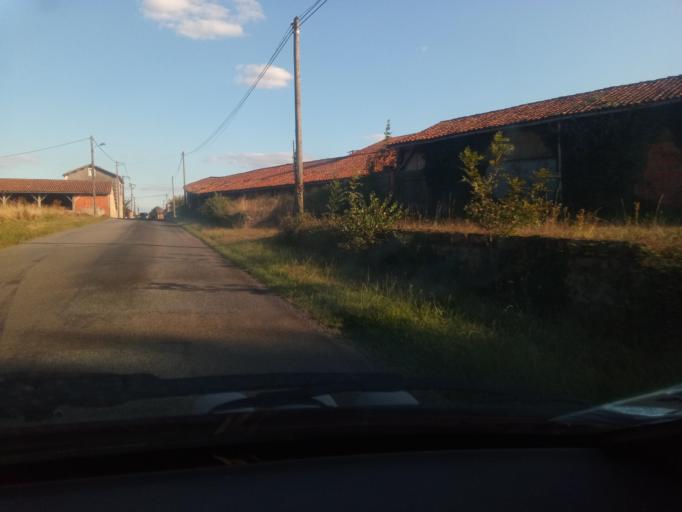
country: FR
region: Poitou-Charentes
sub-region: Departement de la Vienne
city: Availles-Limouzine
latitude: 46.1249
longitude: 0.7262
